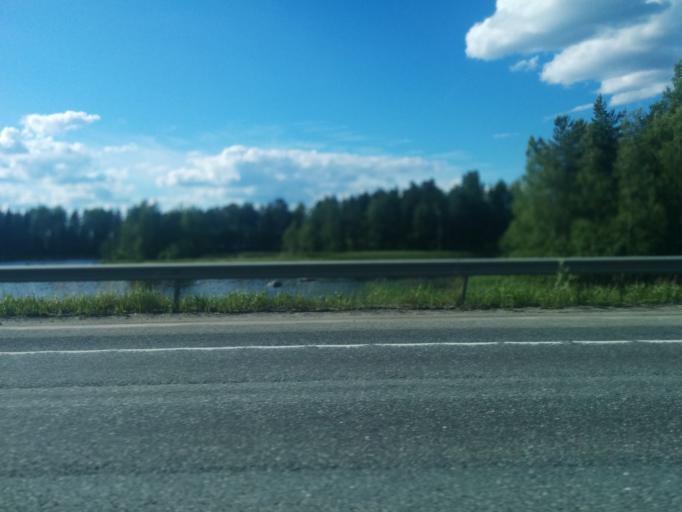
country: FI
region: Pirkanmaa
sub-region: Tampere
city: Tampere
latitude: 61.5267
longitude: 23.9346
